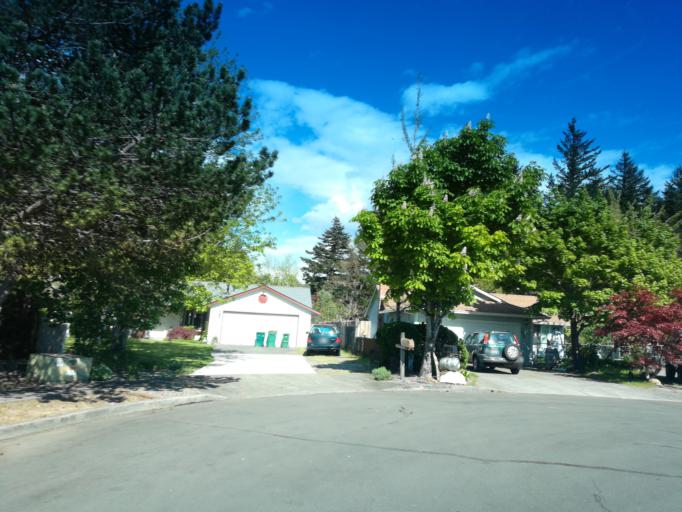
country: US
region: Oregon
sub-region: Multnomah County
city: Troutdale
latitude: 45.5294
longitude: -122.3812
